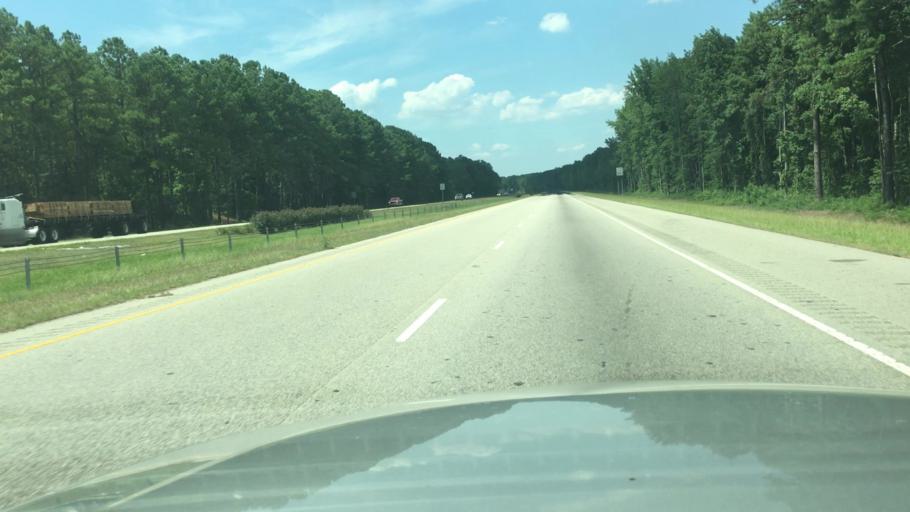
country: US
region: North Carolina
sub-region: Cumberland County
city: Fayetteville
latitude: 34.9875
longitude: -78.8610
